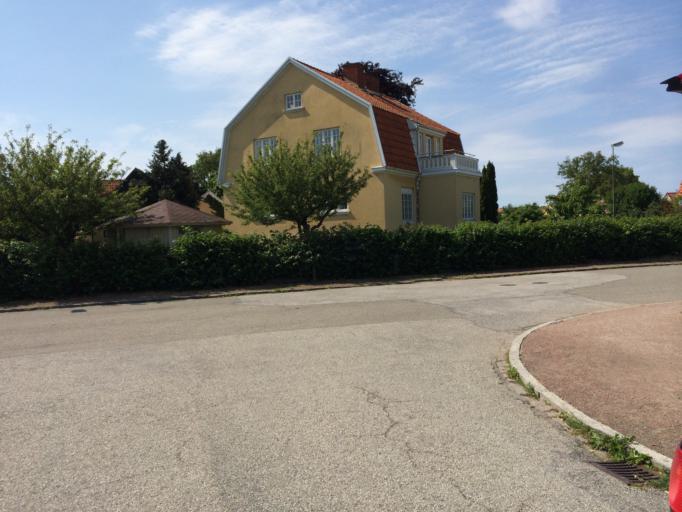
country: SE
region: Skane
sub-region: Malmo
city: Bunkeflostrand
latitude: 55.5760
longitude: 12.9464
